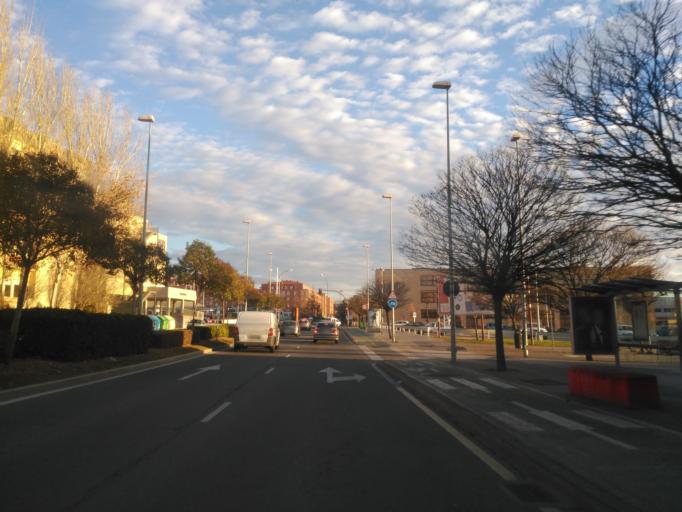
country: ES
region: Castille and Leon
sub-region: Provincia de Salamanca
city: Salamanca
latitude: 40.9706
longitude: -5.6777
